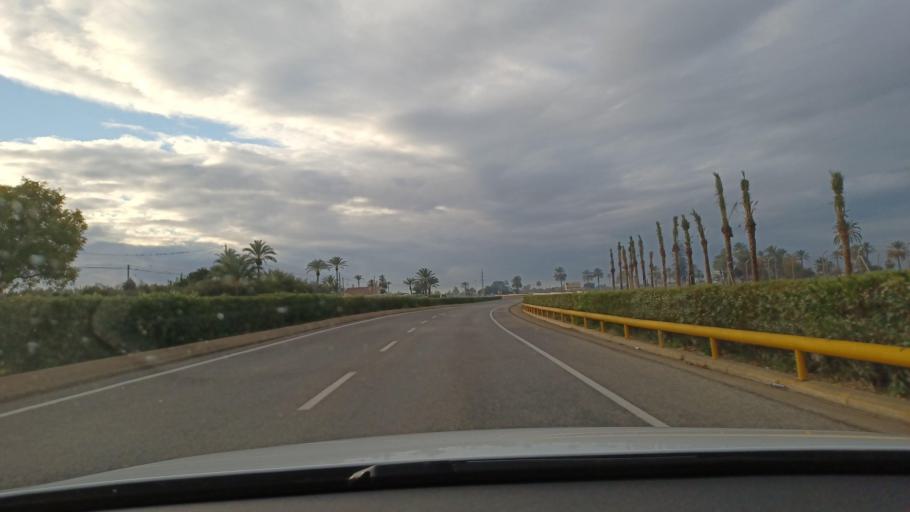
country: ES
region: Valencia
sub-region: Provincia de Alicante
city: Elche
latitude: 38.2363
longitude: -0.7002
